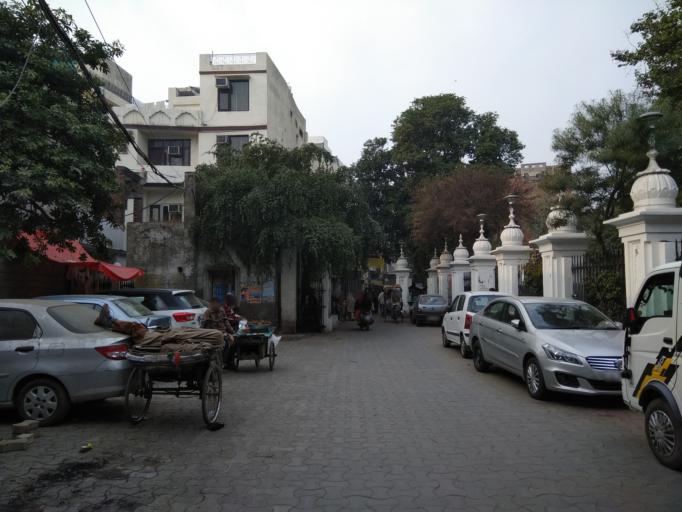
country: IN
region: Punjab
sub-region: Amritsar
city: Amritsar
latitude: 31.6176
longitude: 74.8758
